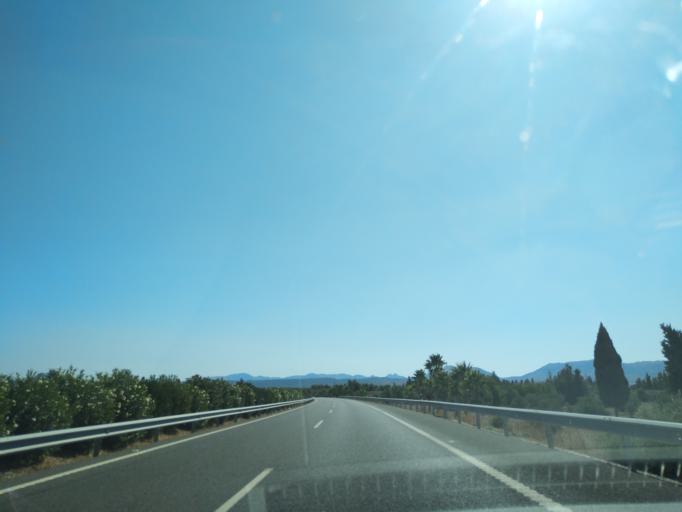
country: ES
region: Andalusia
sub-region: Provincia de Malaga
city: Antequera
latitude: 37.0727
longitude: -4.6043
